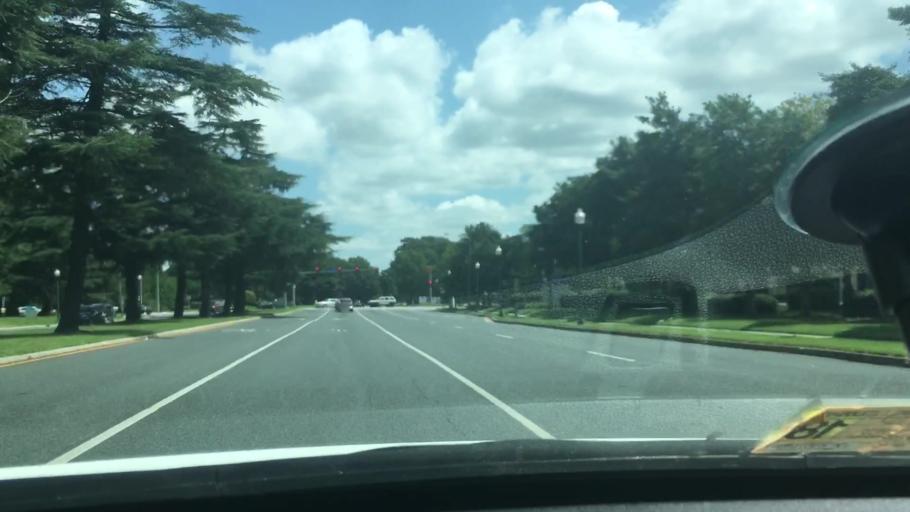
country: US
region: Virginia
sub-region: City of Chesapeake
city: Chesapeake
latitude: 36.7687
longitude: -76.2292
